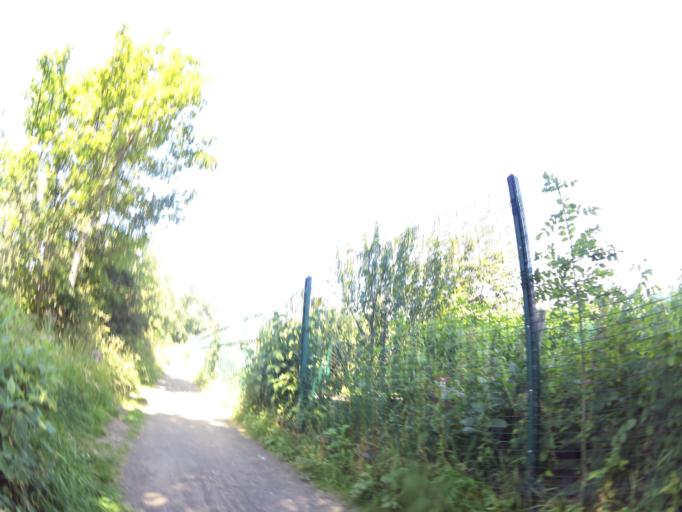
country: GB
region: Scotland
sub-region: Edinburgh
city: Colinton
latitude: 55.9268
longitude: -3.2569
